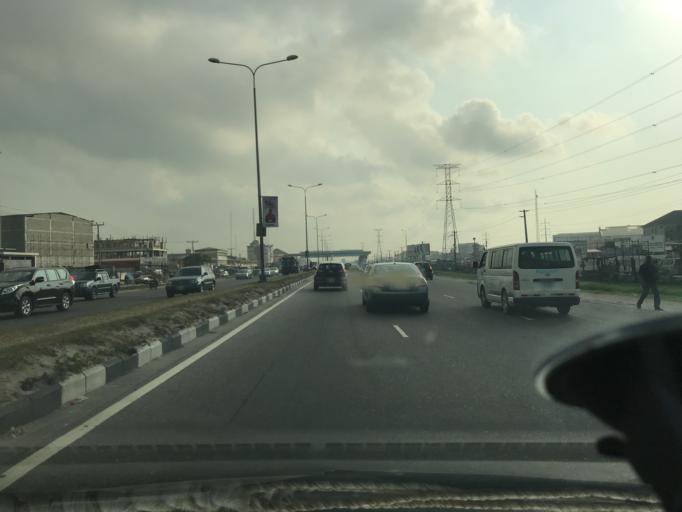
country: NG
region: Lagos
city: Ikoyi
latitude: 6.4374
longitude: 3.5128
